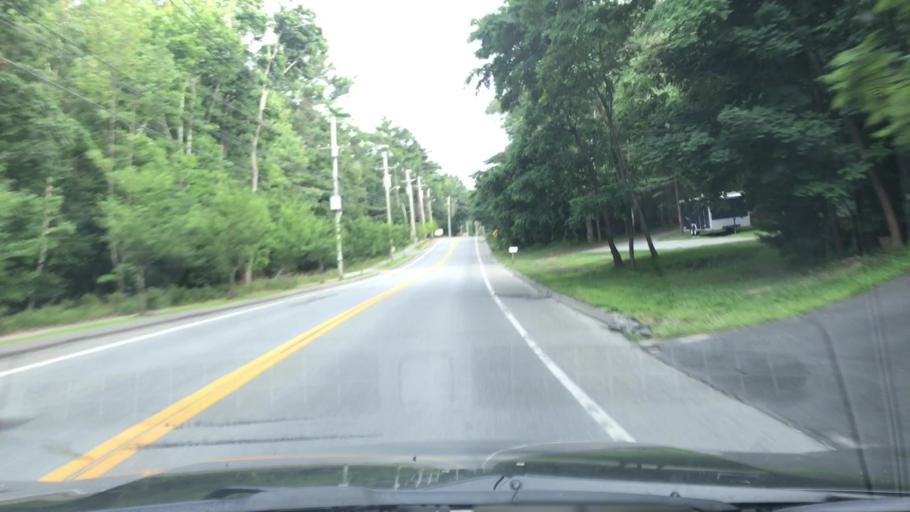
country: US
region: Maine
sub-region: Hancock County
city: Bar Harbor
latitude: 44.3744
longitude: -68.1980
